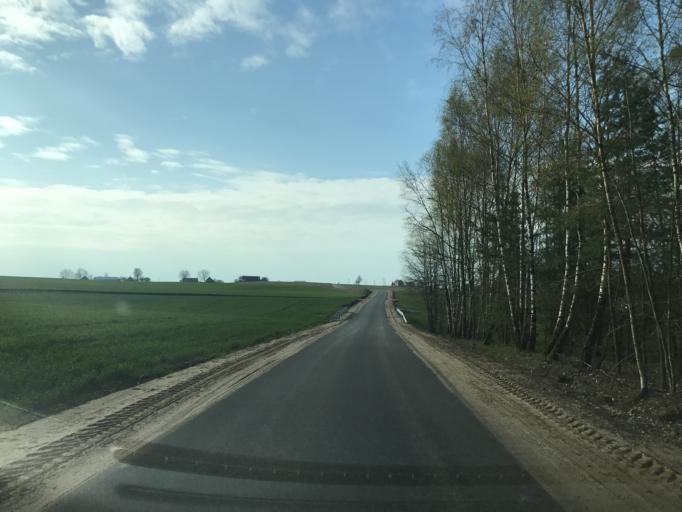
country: PL
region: Warmian-Masurian Voivodeship
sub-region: Powiat dzialdowski
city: Lidzbark
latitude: 53.3244
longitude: 19.8428
